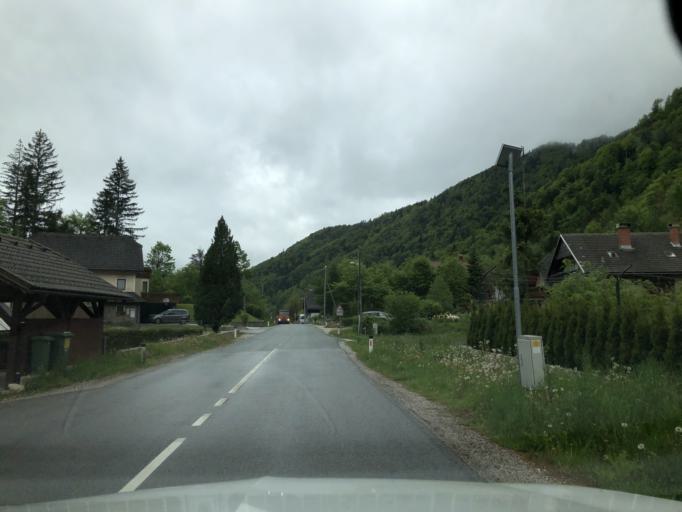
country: SI
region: Jesenice
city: Slovenski Javornik
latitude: 46.4175
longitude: 14.0825
